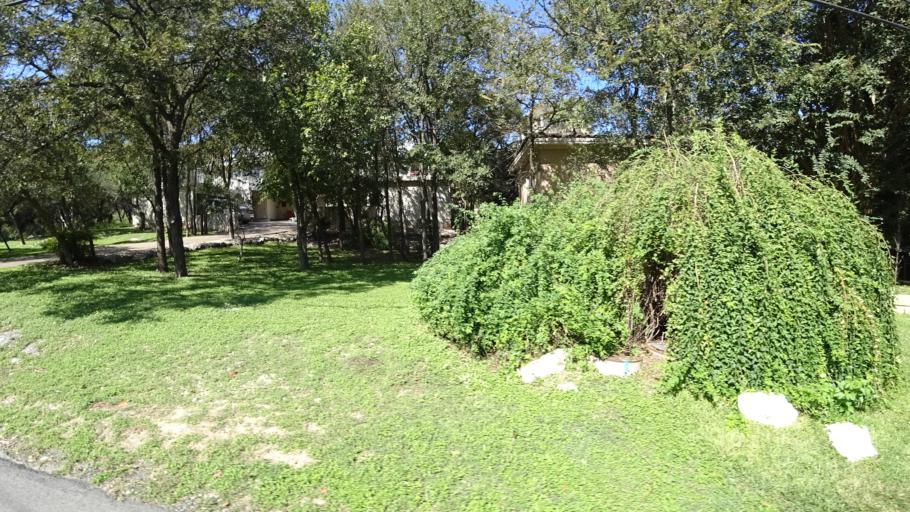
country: US
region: Texas
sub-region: Travis County
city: West Lake Hills
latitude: 30.3008
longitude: -97.7877
